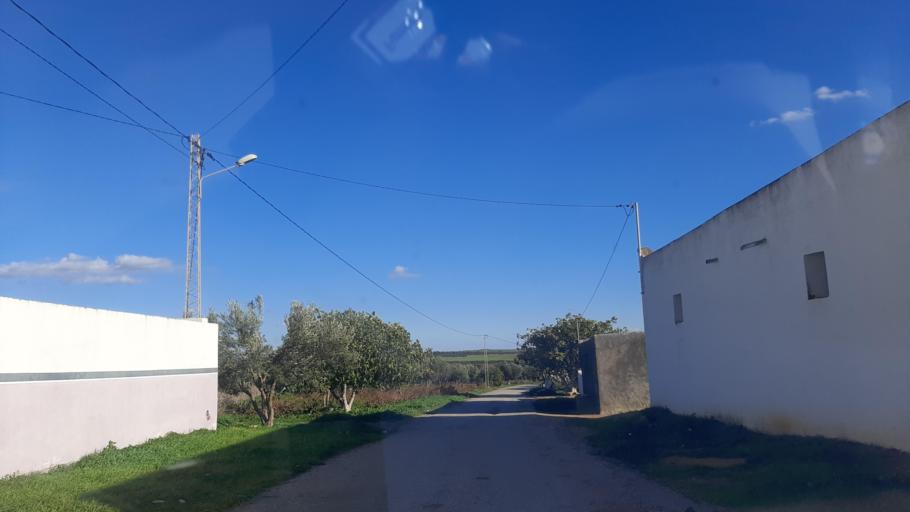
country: TN
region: Nabul
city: El Mida
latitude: 36.8379
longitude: 10.8306
